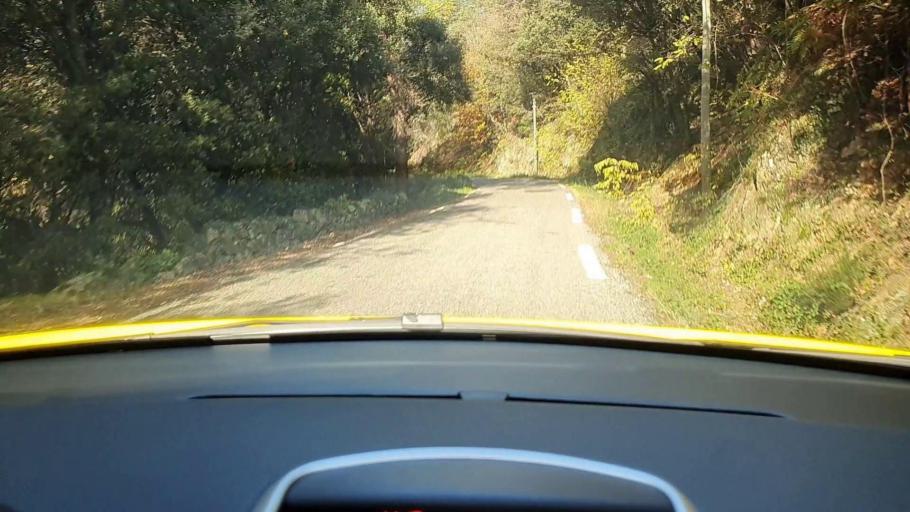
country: FR
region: Languedoc-Roussillon
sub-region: Departement du Gard
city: Lasalle
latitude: 44.0663
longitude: 3.8320
